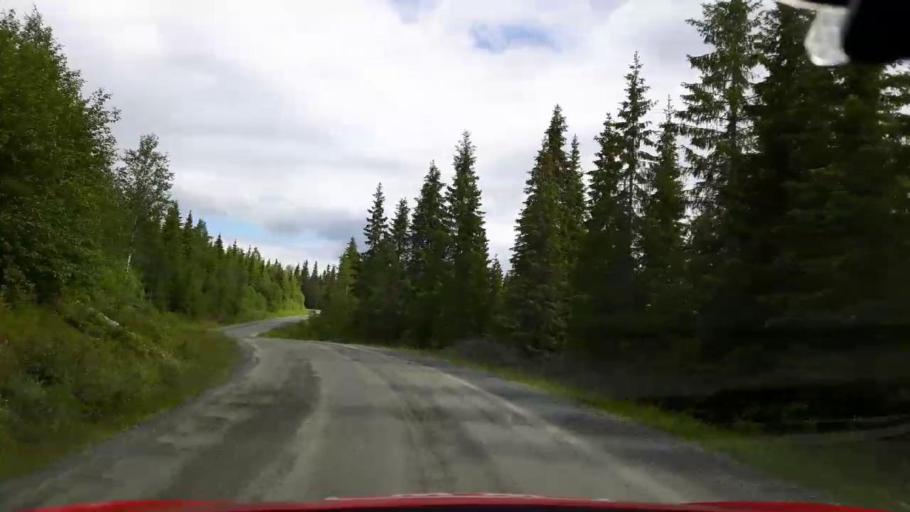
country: NO
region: Nord-Trondelag
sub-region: Lierne
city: Sandvika
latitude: 64.1442
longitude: 13.9099
